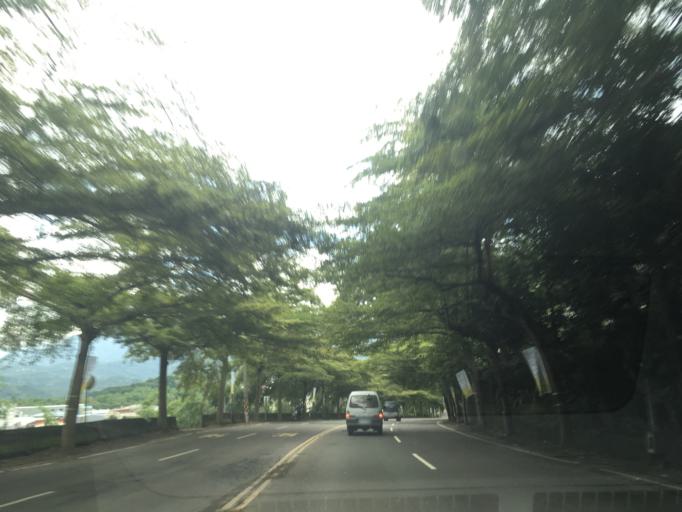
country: TW
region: Taiwan
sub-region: Yunlin
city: Douliu
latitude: 23.5924
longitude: 120.5340
